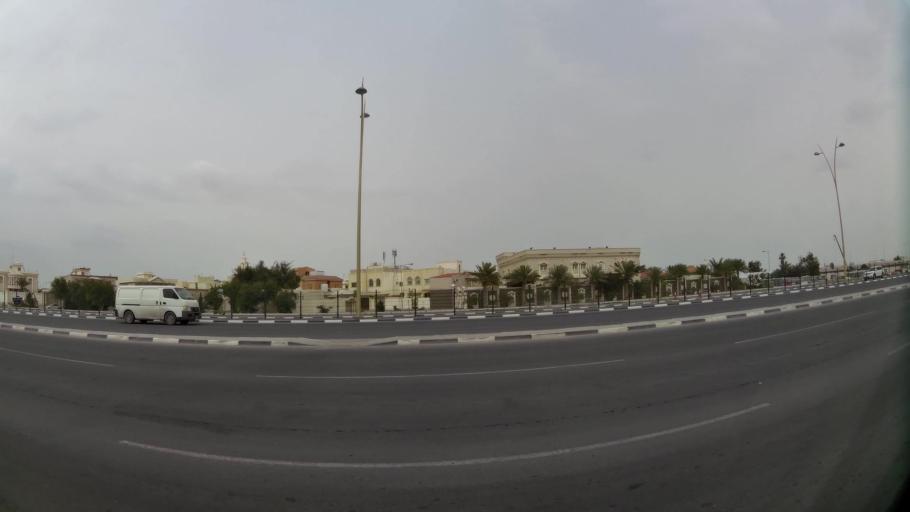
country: QA
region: Baladiyat ad Dawhah
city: Doha
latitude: 25.2406
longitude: 51.5461
